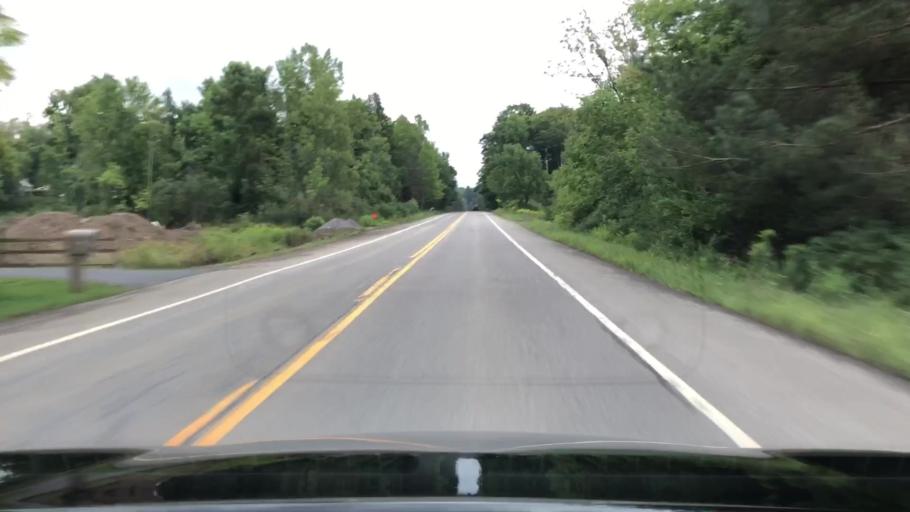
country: US
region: New York
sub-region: Erie County
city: Orchard Park
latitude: 42.7609
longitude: -78.6969
